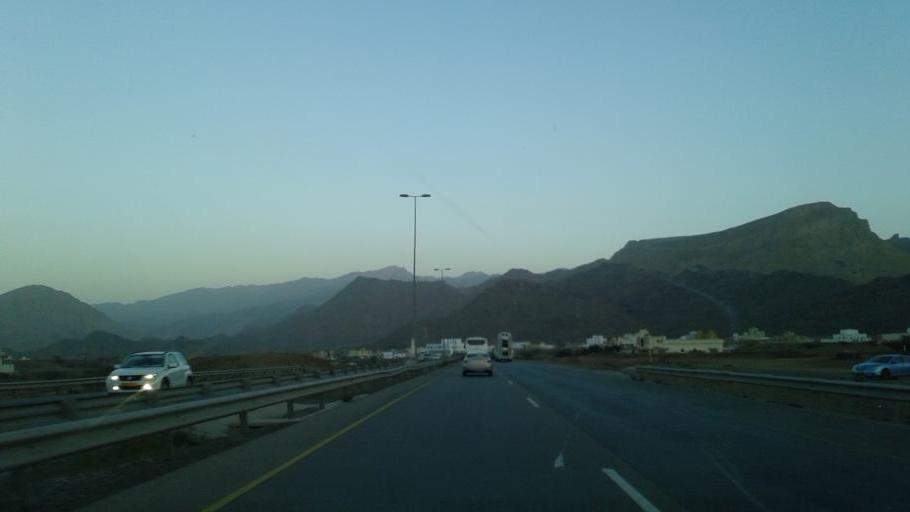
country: OM
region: Muhafazat ad Dakhiliyah
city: Bidbid
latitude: 23.4604
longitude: 58.1660
